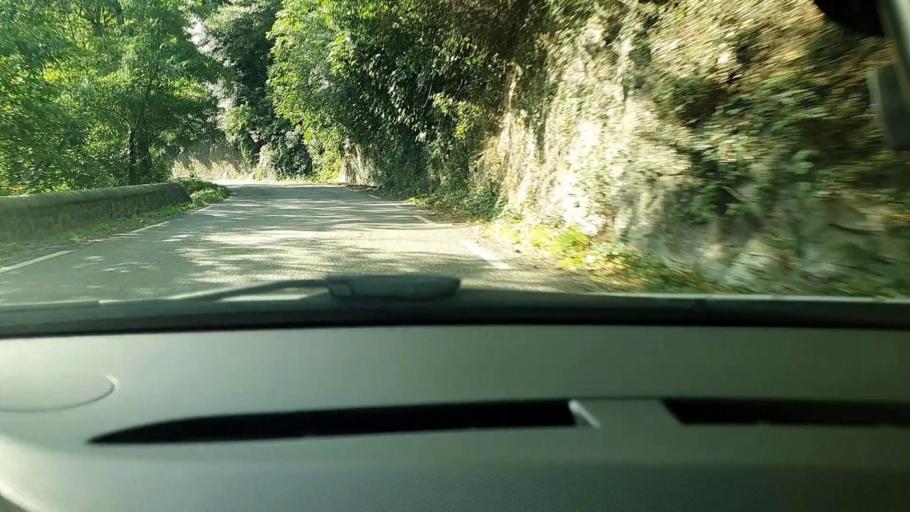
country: FR
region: Languedoc-Roussillon
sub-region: Departement du Gard
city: Besseges
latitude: 44.2921
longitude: 4.0634
